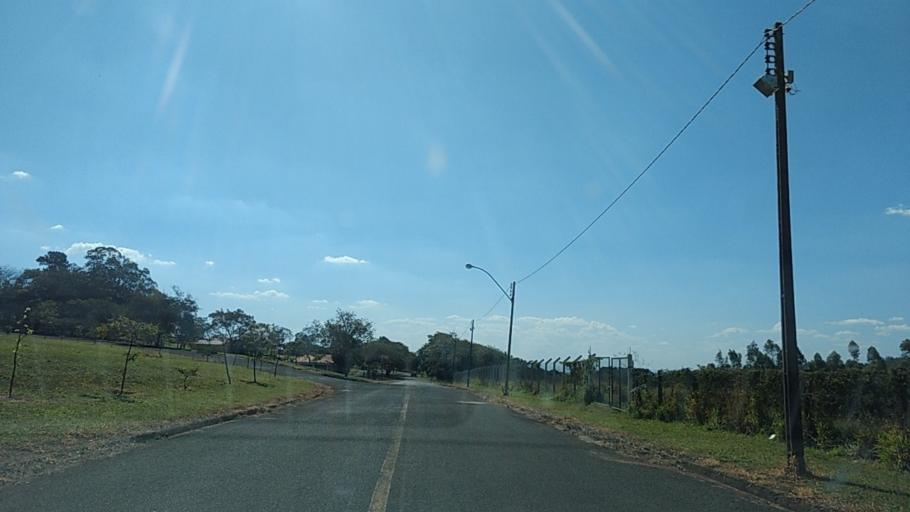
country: BR
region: Sao Paulo
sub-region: Botucatu
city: Botucatu
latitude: -22.8468
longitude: -48.4327
